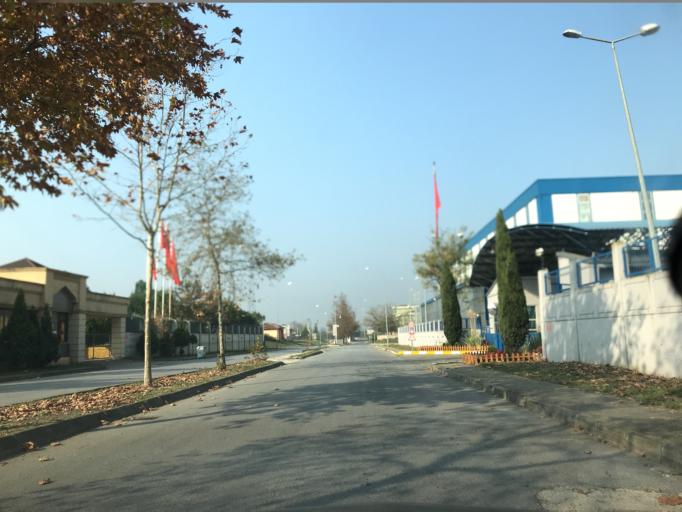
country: TR
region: Duzce
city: Duzce
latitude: 40.7882
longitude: 31.1342
